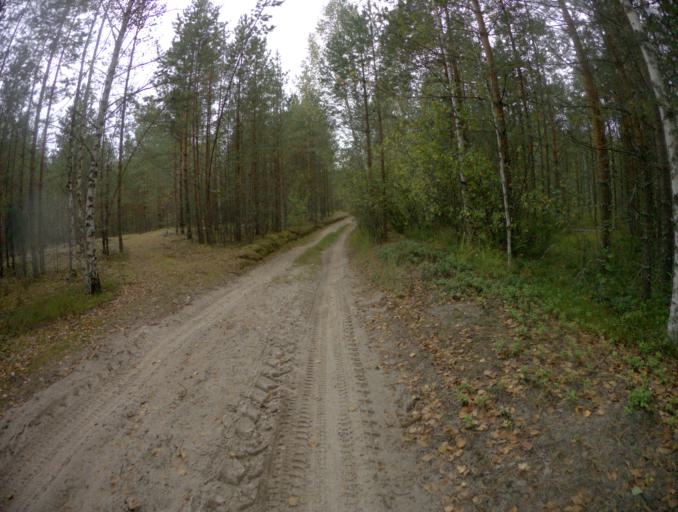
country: RU
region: Vladimir
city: Golovino
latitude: 55.8741
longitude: 40.3974
